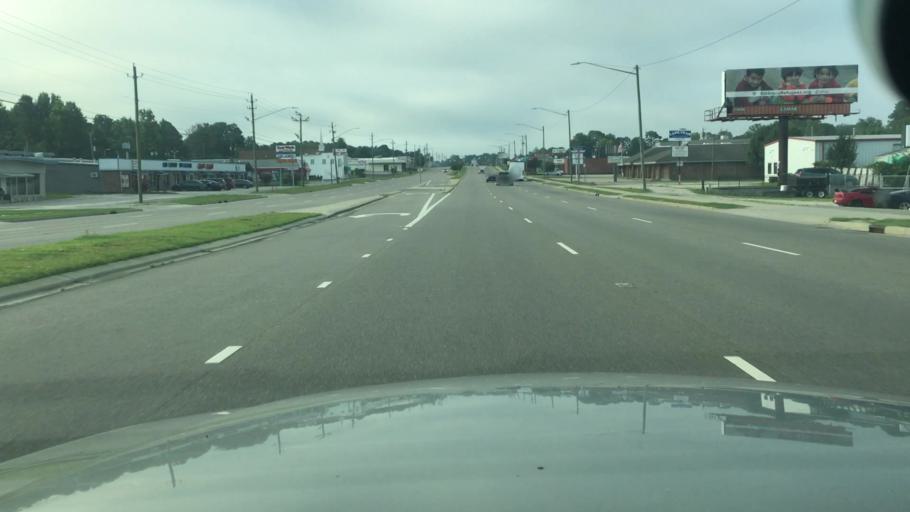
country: US
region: North Carolina
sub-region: Cumberland County
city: Fort Bragg
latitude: 35.0980
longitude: -78.9569
